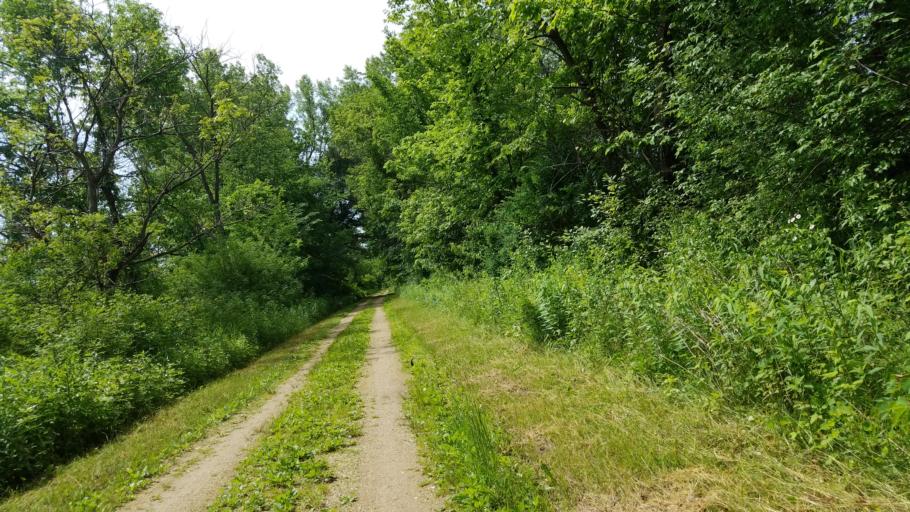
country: US
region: Wisconsin
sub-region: Dunn County
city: Menomonie
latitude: 44.7992
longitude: -91.9471
